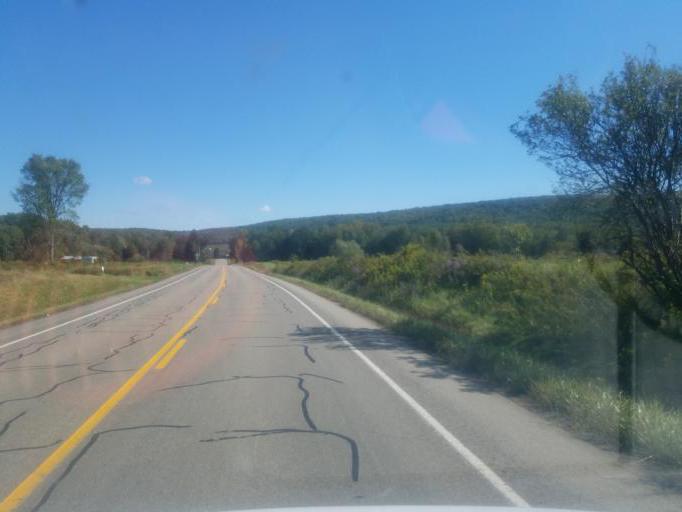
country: US
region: New York
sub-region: Allegany County
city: Friendship
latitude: 42.2999
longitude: -78.1589
